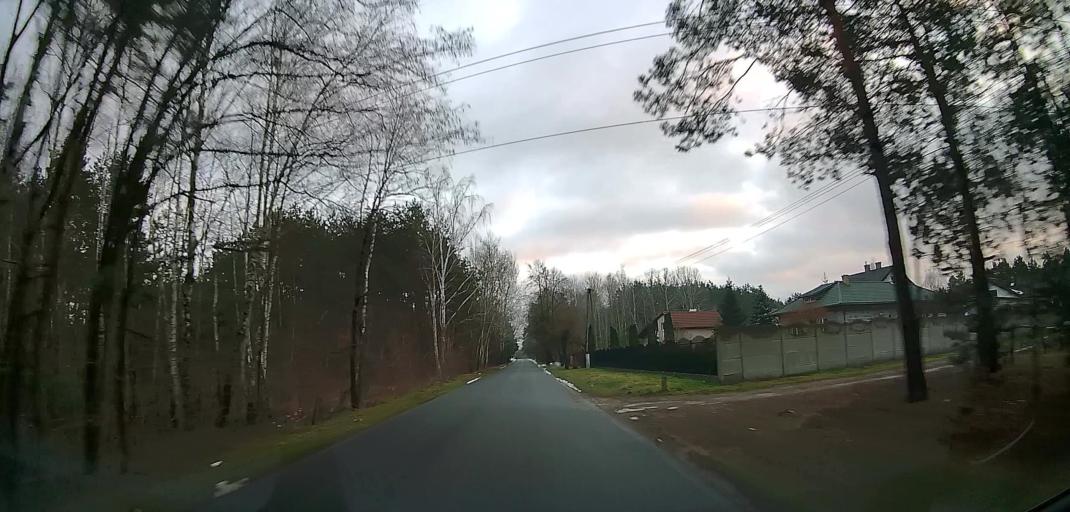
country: PL
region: Masovian Voivodeship
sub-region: Radom
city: Radom
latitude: 51.4530
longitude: 21.1289
